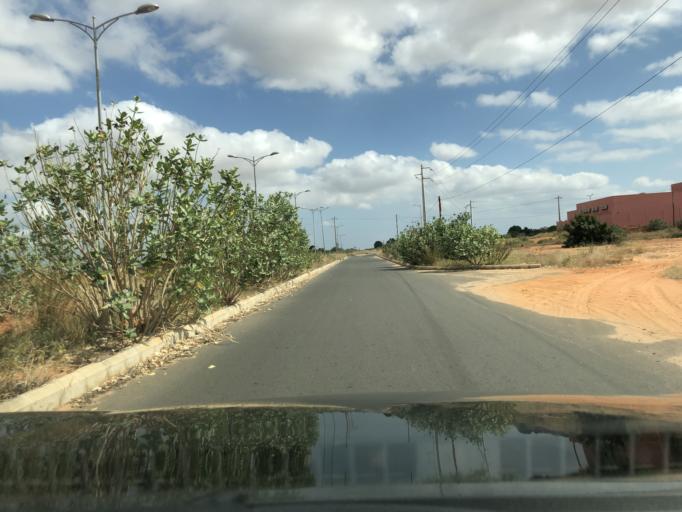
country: AO
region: Luanda
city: Luanda
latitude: -8.9594
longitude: 13.2402
